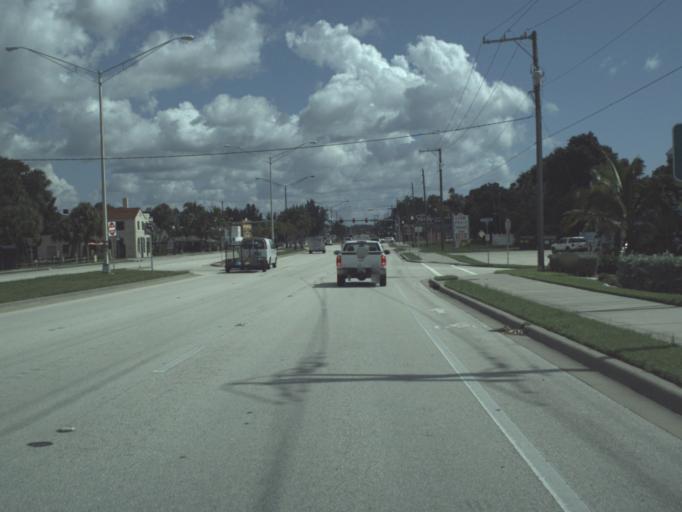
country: US
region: Florida
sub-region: Sarasota County
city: Nokomis
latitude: 27.1179
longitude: -82.4509
